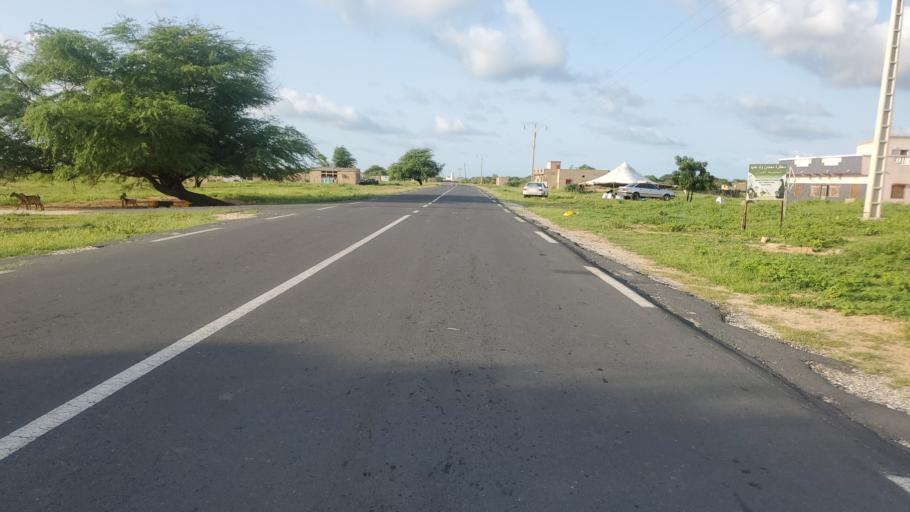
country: SN
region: Saint-Louis
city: Saint-Louis
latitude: 16.1366
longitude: -16.4110
